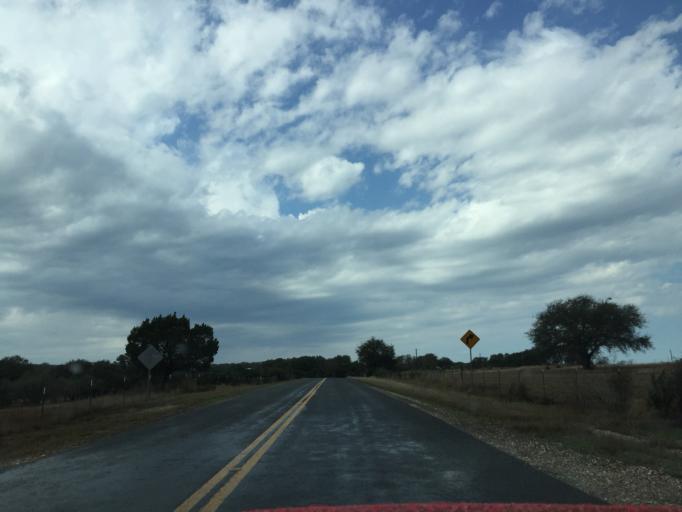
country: US
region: Texas
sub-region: Burnet County
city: Bertram
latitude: 30.6261
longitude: -97.9855
